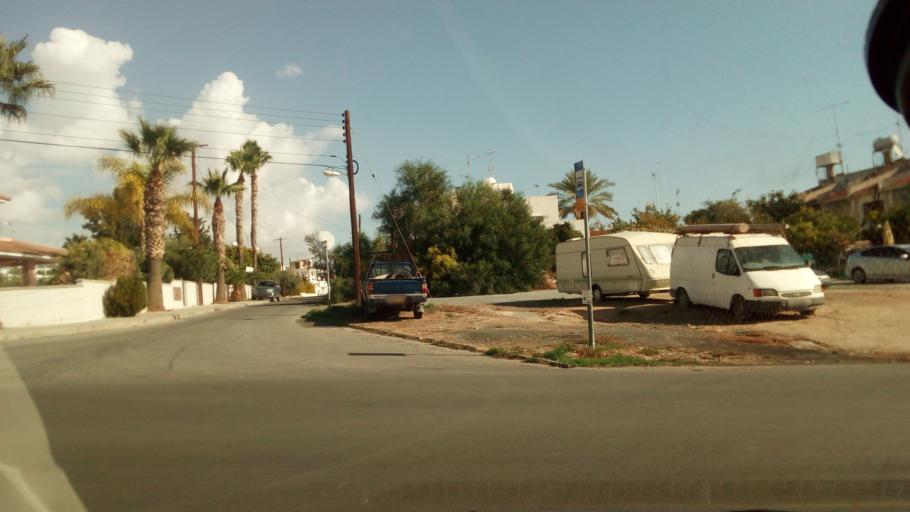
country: CY
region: Larnaka
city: Larnaca
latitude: 34.9128
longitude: 33.6114
